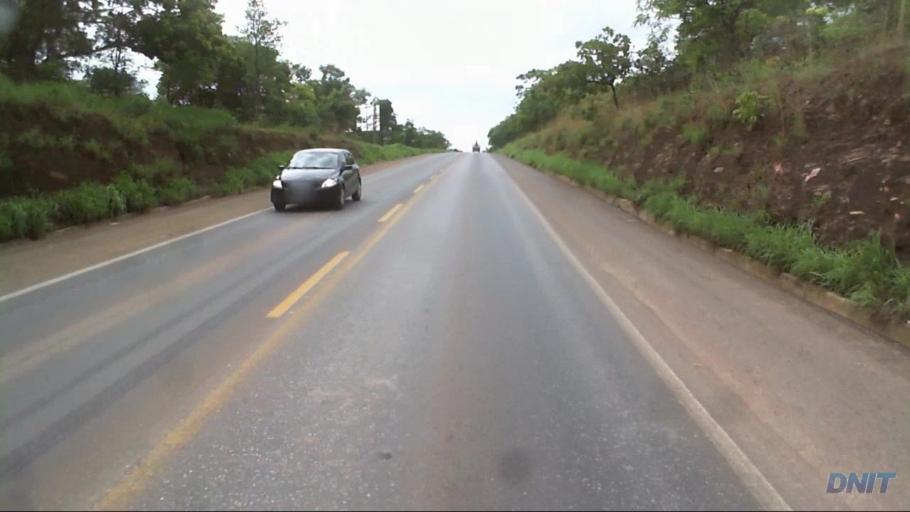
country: BR
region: Goias
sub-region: Uruacu
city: Uruacu
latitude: -14.5589
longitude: -49.1576
